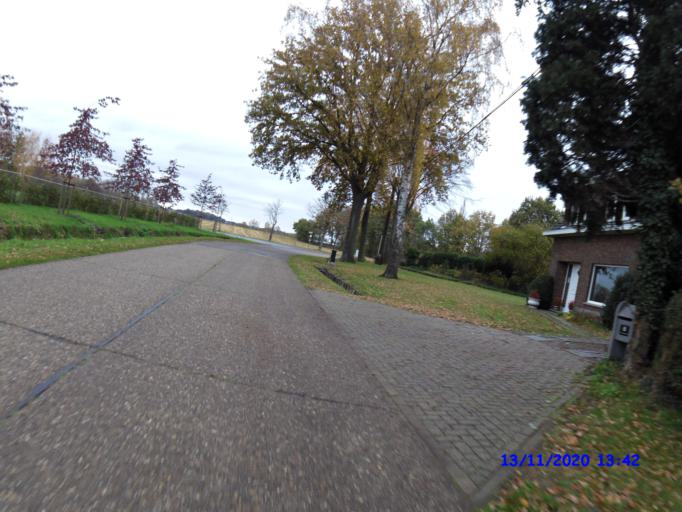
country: BE
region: Flanders
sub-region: Provincie Antwerpen
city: Kasterlee
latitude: 51.2574
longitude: 4.9879
